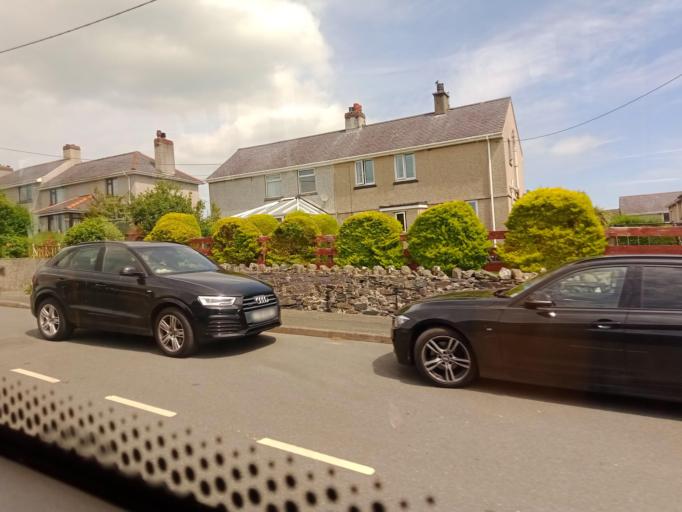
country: GB
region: Wales
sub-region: Gwynedd
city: Bangor
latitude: 53.2438
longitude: -4.1481
